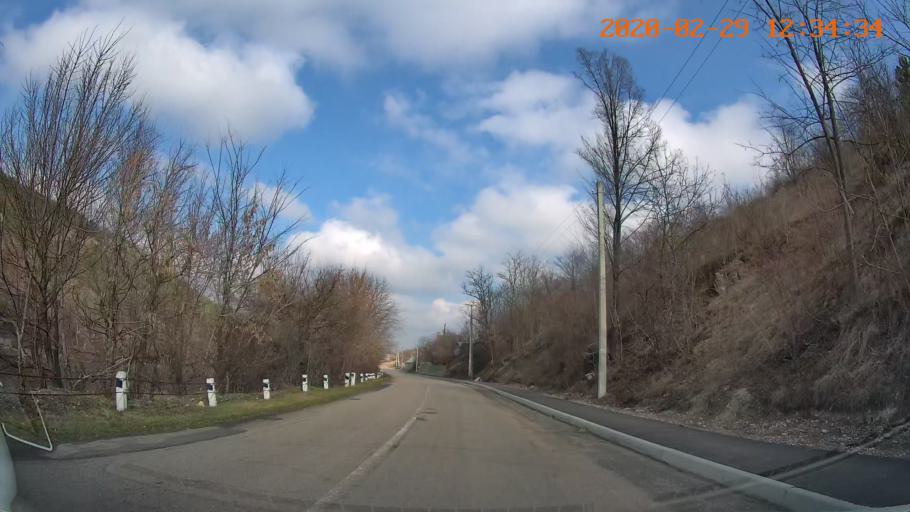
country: MD
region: Telenesti
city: Camenca
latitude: 48.0402
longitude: 28.7150
